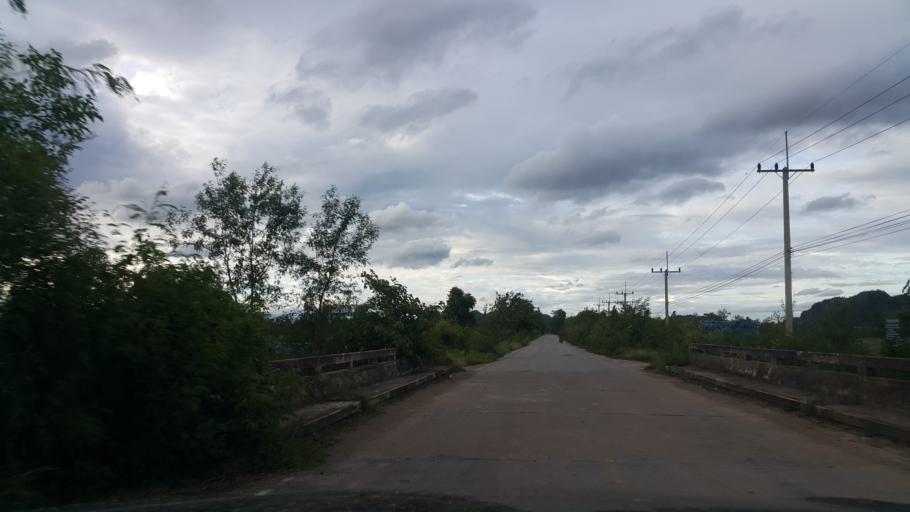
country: TH
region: Sukhothai
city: Thung Saliam
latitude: 17.1672
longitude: 99.5239
